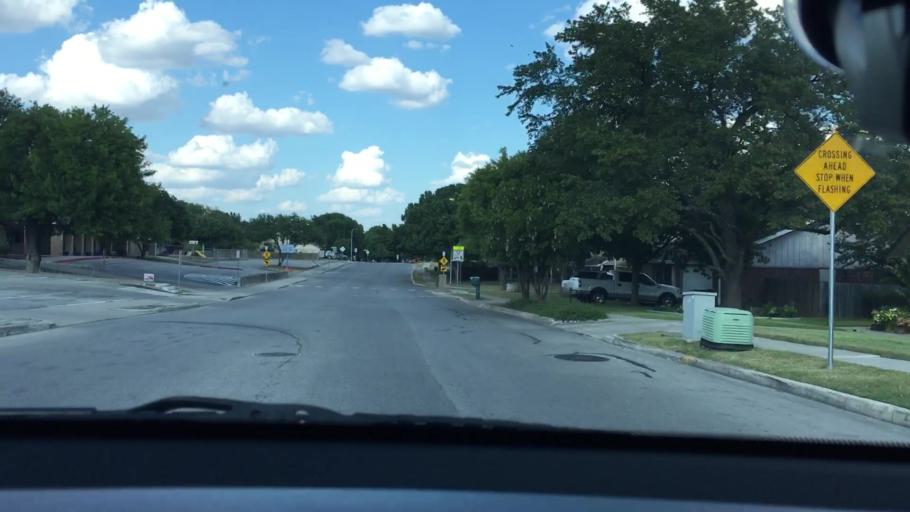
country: US
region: Texas
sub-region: Bexar County
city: Live Oak
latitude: 29.5677
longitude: -98.3186
